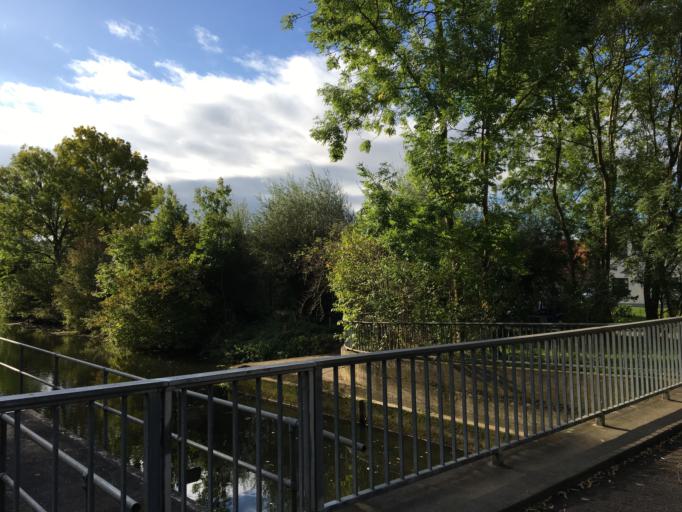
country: DE
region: Lower Saxony
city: Braunschweig
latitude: 52.2892
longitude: 10.4995
